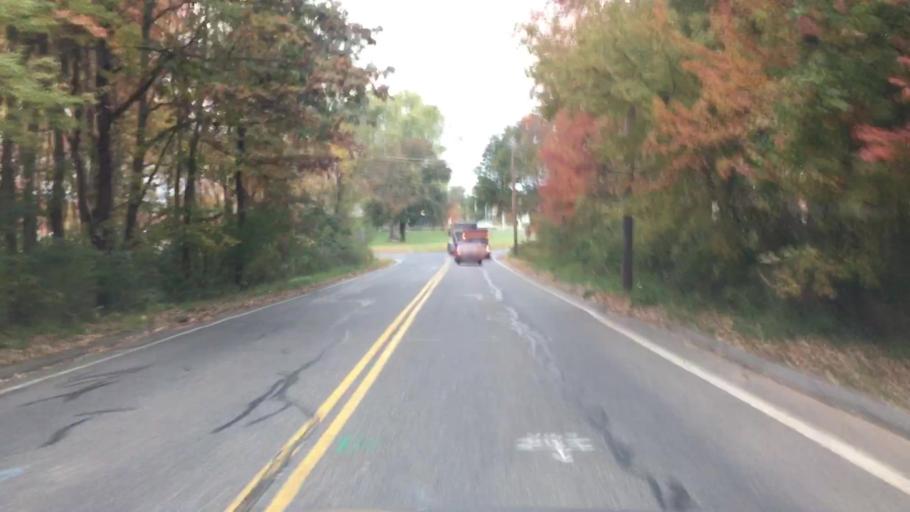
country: US
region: Massachusetts
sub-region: Hampden County
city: East Longmeadow
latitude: 42.0412
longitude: -72.5167
